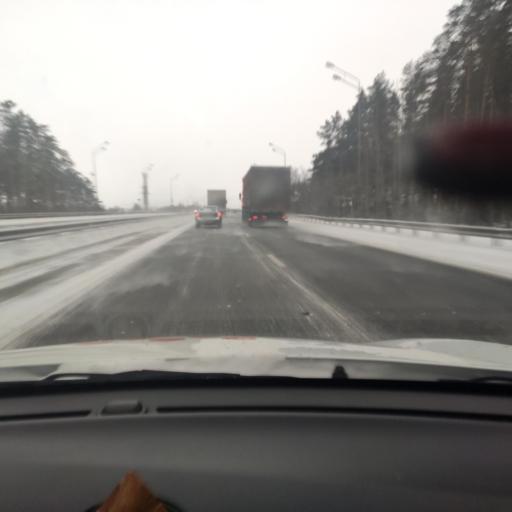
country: RU
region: Tatarstan
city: Osinovo
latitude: 55.8269
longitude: 48.8478
